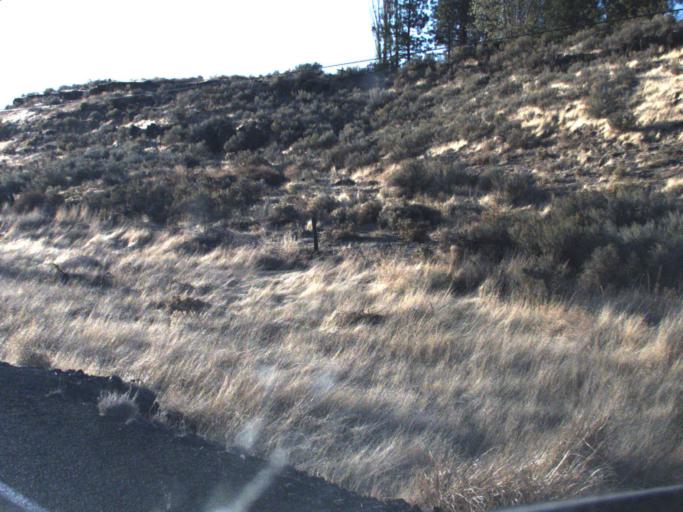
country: US
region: Washington
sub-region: Franklin County
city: Connell
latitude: 46.6454
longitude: -118.5490
